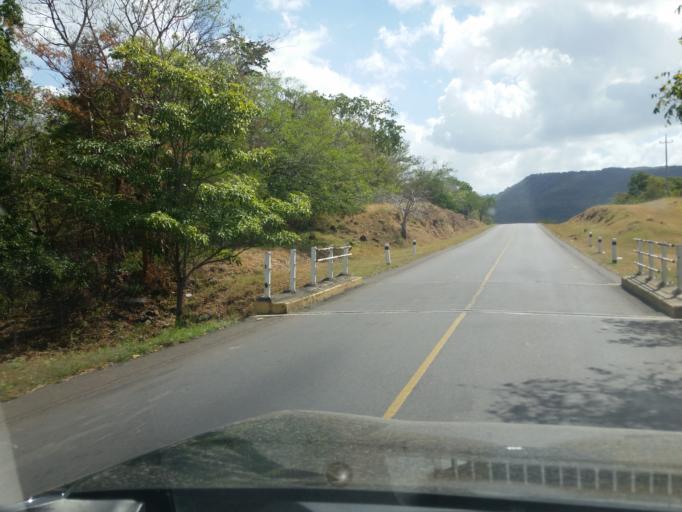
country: NI
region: Chontales
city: Comalapa
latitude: 12.2013
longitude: -85.6256
